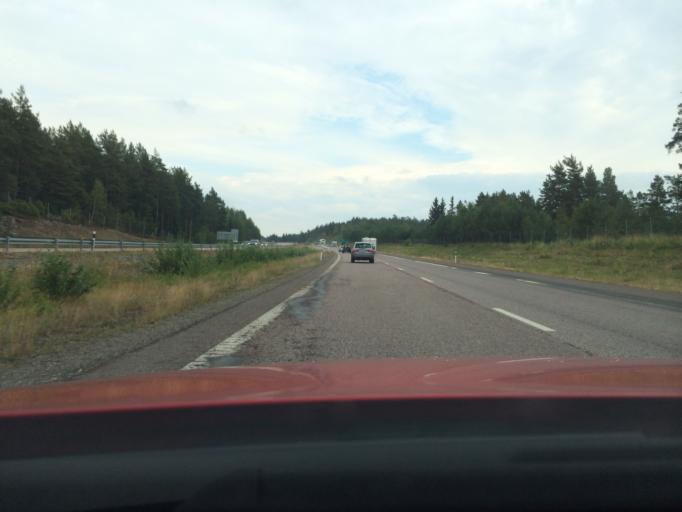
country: SE
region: Soedermanland
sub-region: Nykopings Kommun
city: Olstorp
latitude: 58.7551
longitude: 16.6368
